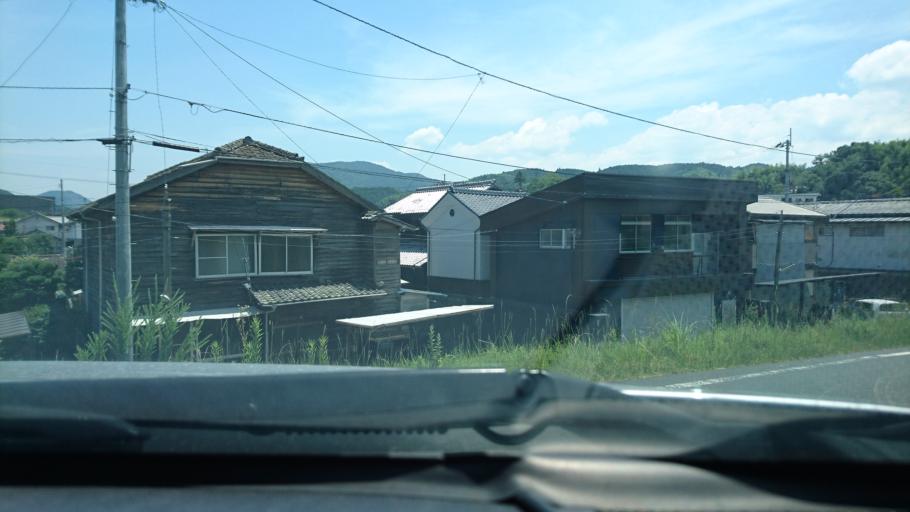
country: JP
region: Ehime
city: Ozu
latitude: 33.5096
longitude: 132.5378
